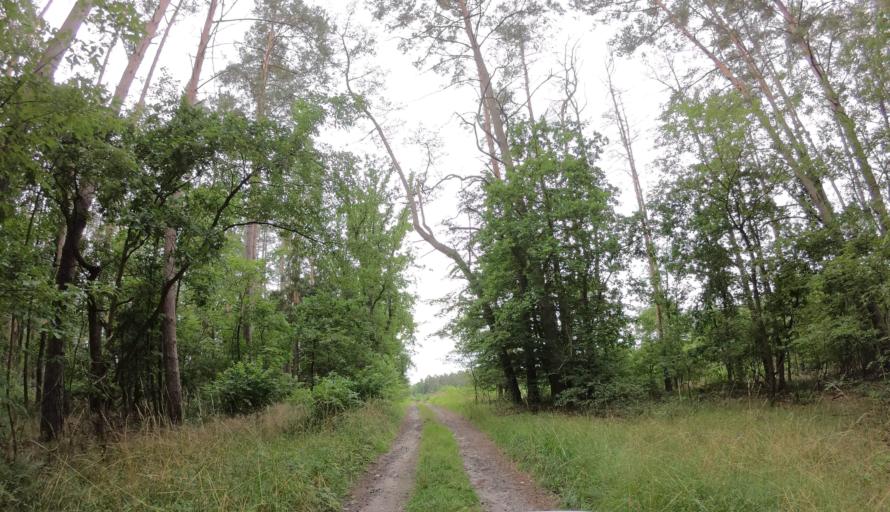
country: PL
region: West Pomeranian Voivodeship
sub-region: Powiat goleniowski
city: Przybiernow
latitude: 53.8306
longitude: 14.7441
